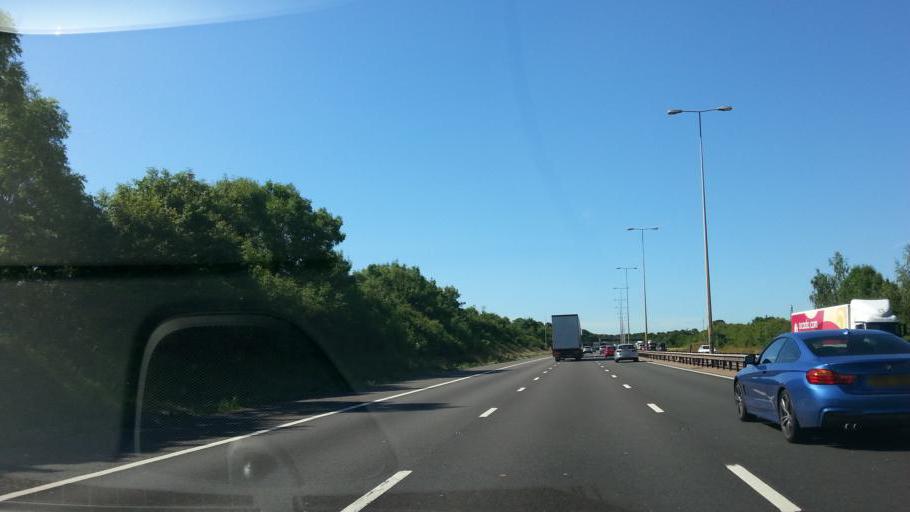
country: GB
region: England
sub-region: Worcestershire
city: Kempsey
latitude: 52.1390
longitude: -2.1967
